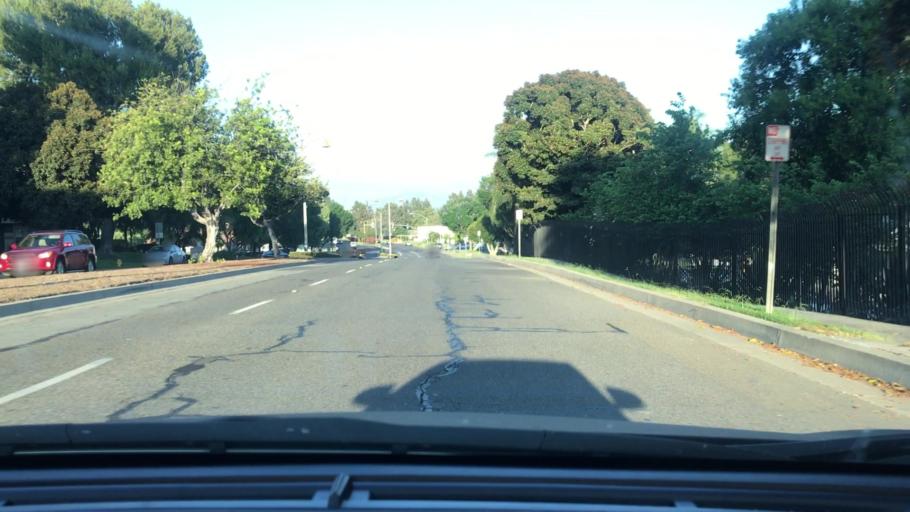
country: US
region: California
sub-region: Orange County
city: Placentia
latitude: 33.8713
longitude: -117.8654
